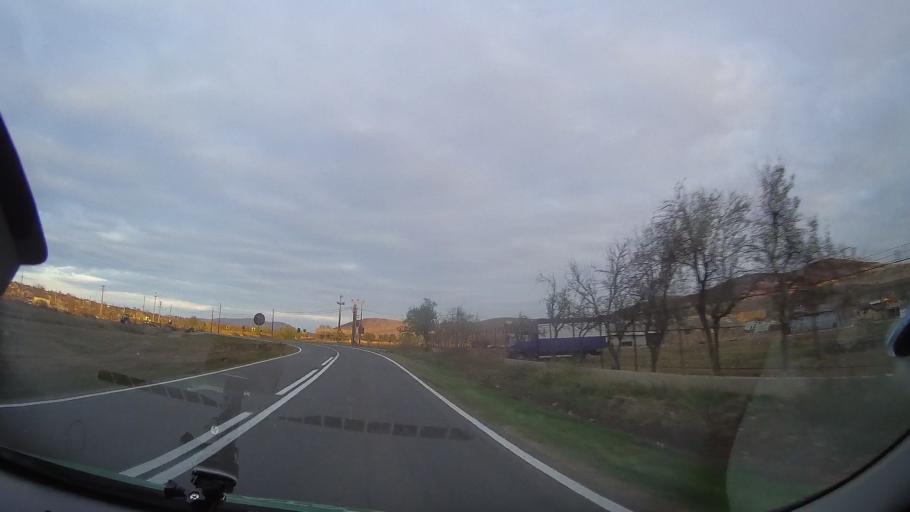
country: RO
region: Tulcea
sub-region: Comuna Nalbant
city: Nicolae Balcescu
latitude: 44.9923
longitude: 28.5698
